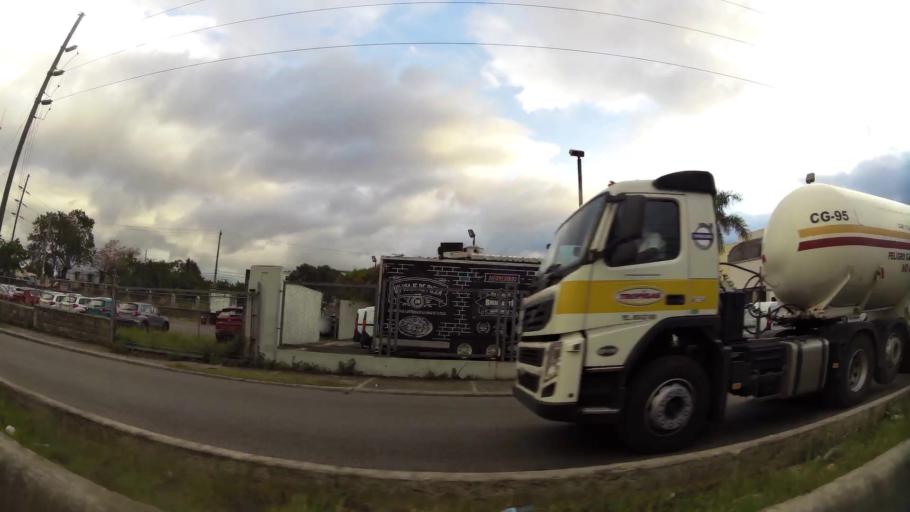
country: DO
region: Nacional
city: Santo Domingo
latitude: 18.5073
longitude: -69.9902
